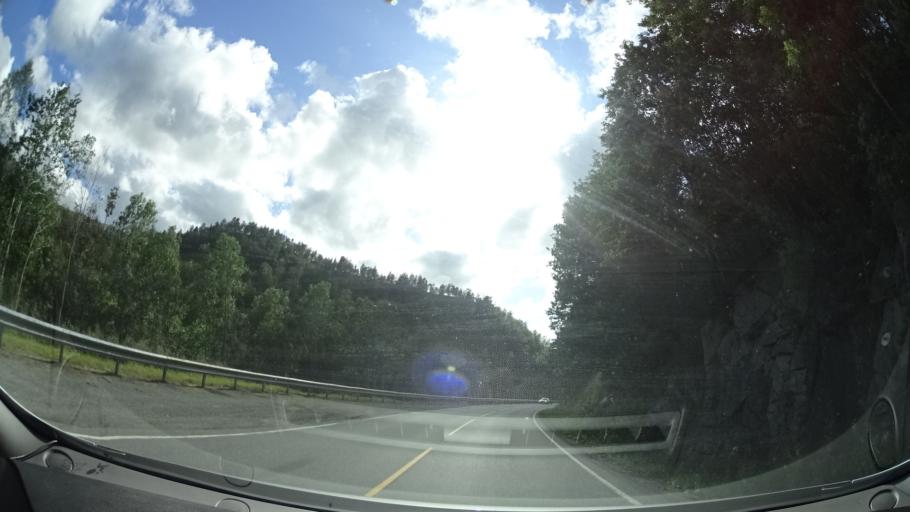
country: NO
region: Sor-Trondelag
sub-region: Hemne
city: Kyrksaeterora
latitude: 63.2151
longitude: 9.1261
